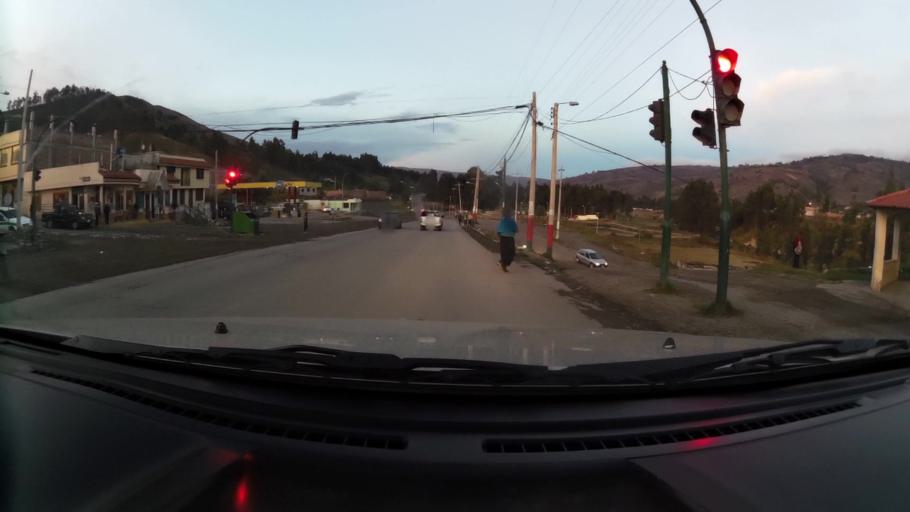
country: EC
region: Chimborazo
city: Riobamba
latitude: -1.9323
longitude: -78.7059
